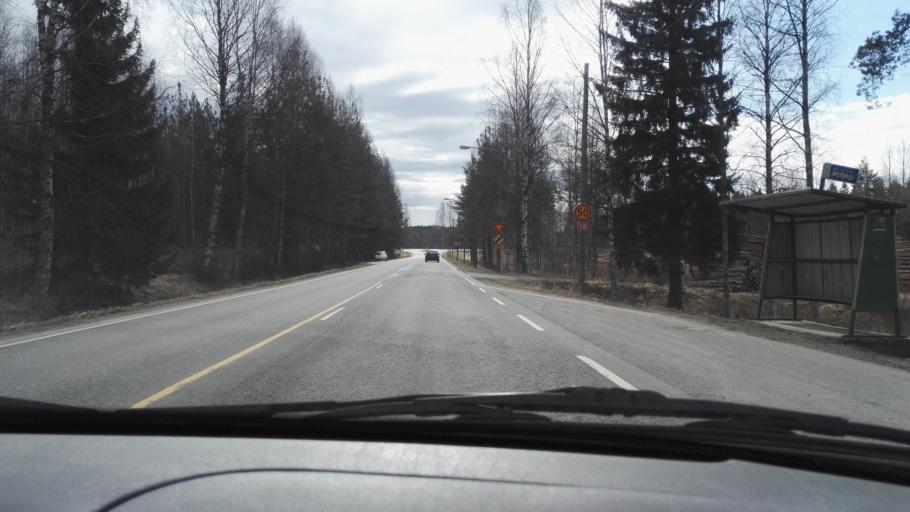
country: FI
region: Central Finland
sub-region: Jyvaeskylae
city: Petaejaevesi
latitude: 62.2590
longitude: 25.1936
